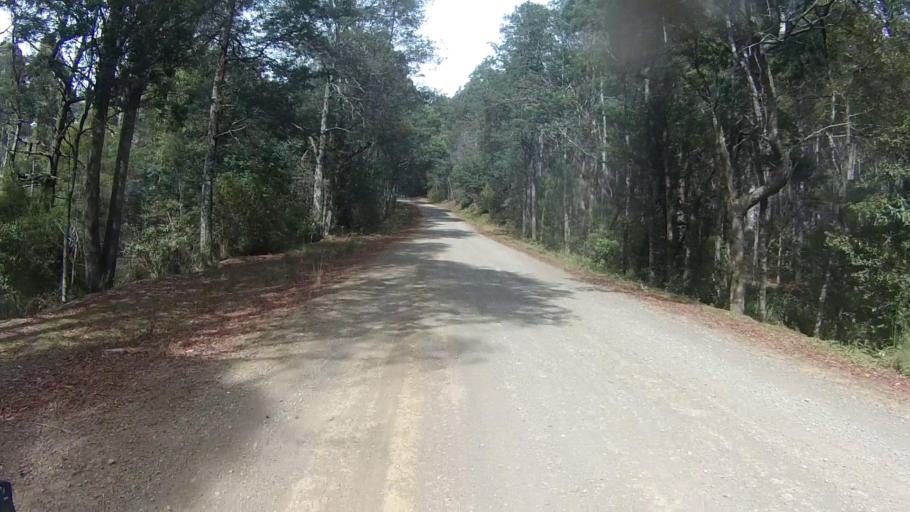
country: AU
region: Tasmania
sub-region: Sorell
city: Sorell
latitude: -42.6931
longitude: 147.8617
